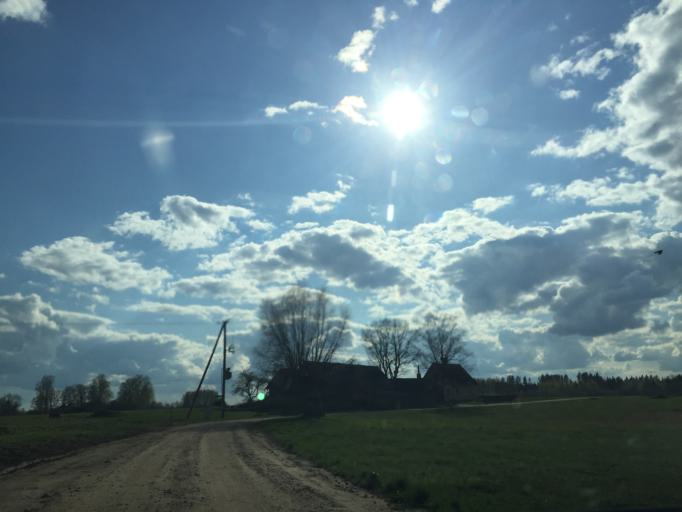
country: LV
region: Beverina
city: Murmuiza
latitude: 57.4090
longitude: 25.5206
